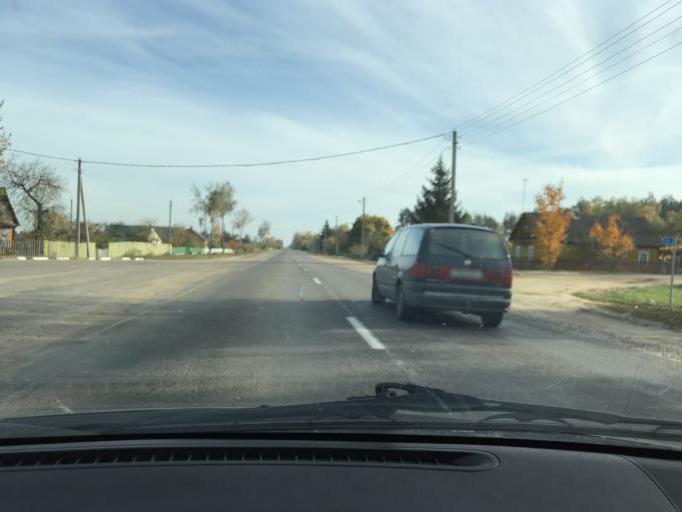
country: BY
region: Brest
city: Asnyezhytsy
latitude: 52.2241
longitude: 26.0278
